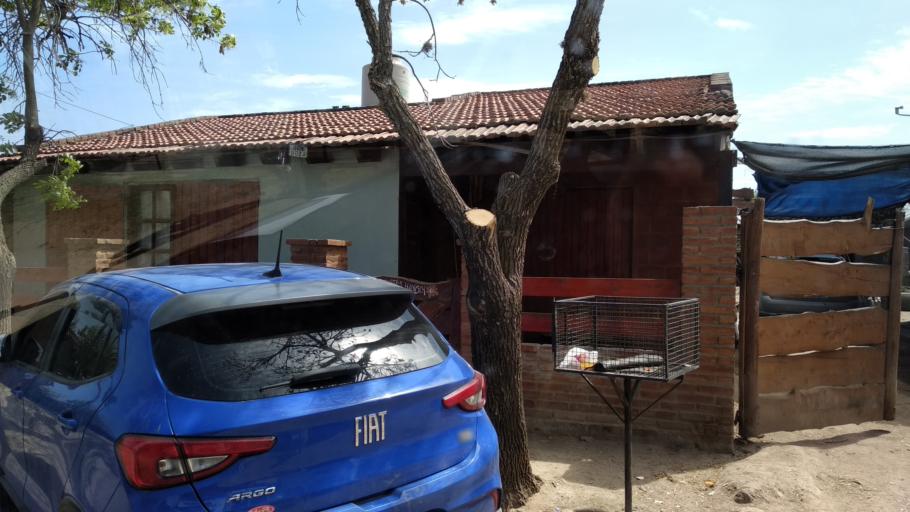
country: AR
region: Cordoba
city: Mina Clavero
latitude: -31.7312
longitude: -65.0156
